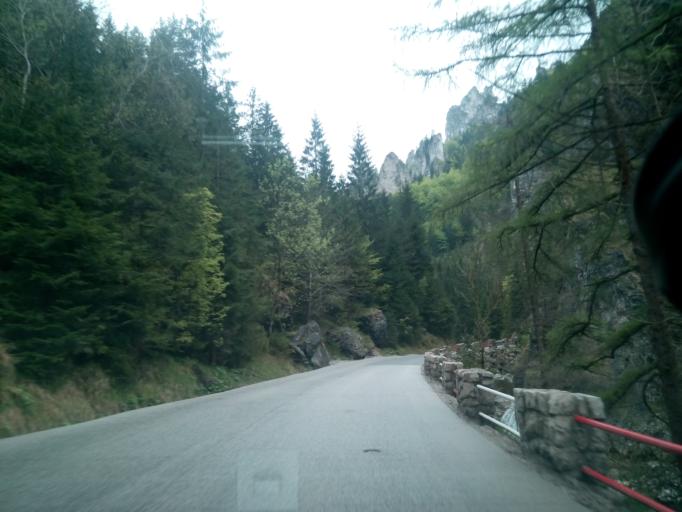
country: SK
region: Zilinsky
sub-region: Okres Zilina
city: Terchova
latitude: 49.2467
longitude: 19.0395
